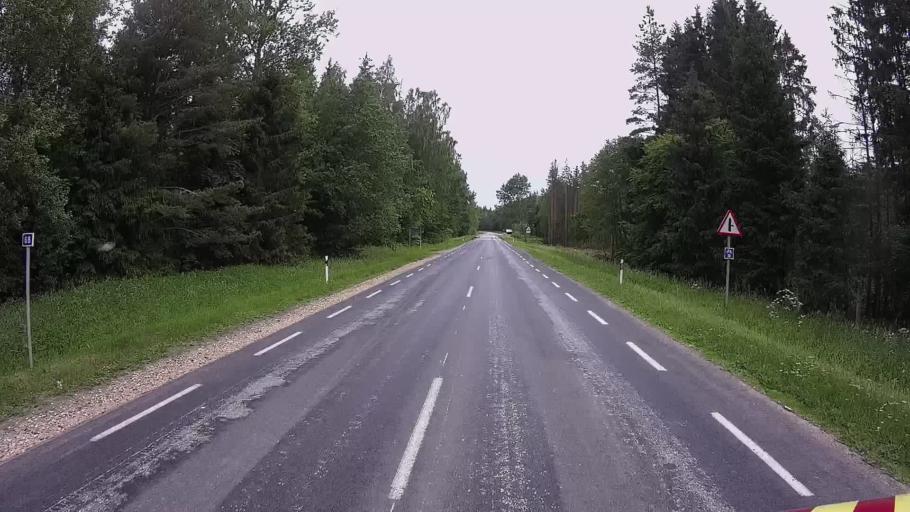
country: EE
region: Viljandimaa
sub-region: Karksi vald
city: Karksi-Nuia
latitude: 58.2061
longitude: 25.6208
